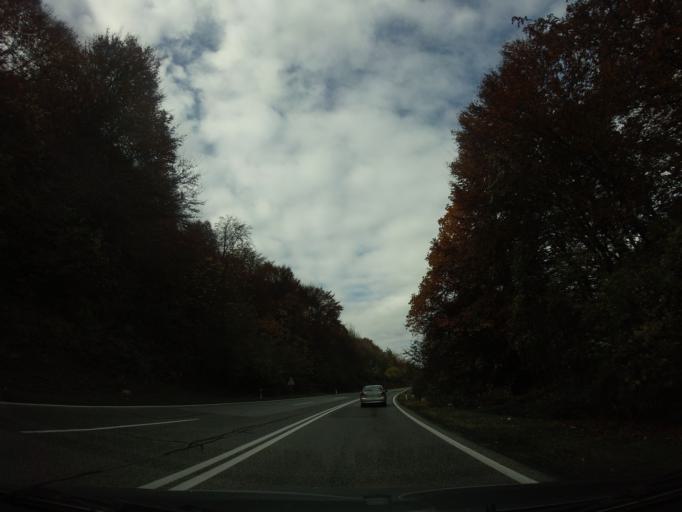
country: HR
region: Karlovacka
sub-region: Grad Karlovac
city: Slunj
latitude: 45.0711
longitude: 15.5896
